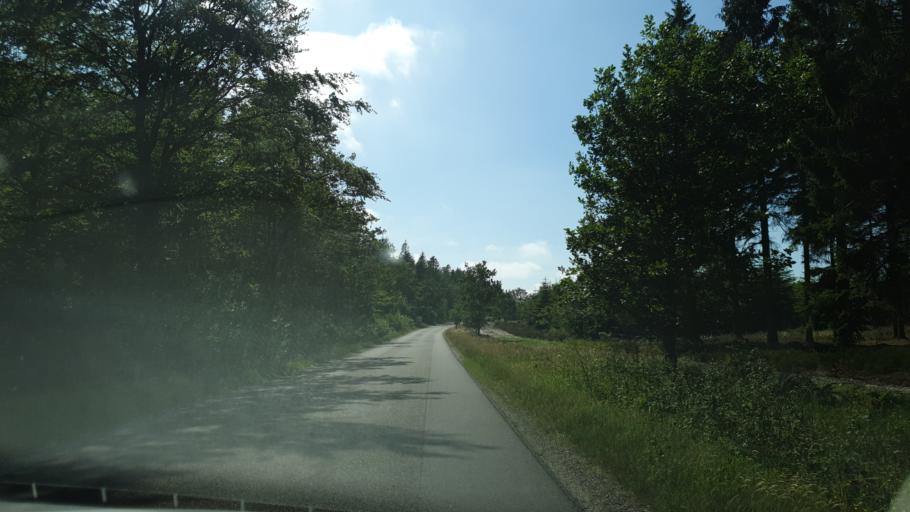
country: DK
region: Central Jutland
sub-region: Ringkobing-Skjern Kommune
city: Skjern
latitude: 55.9994
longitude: 8.4528
